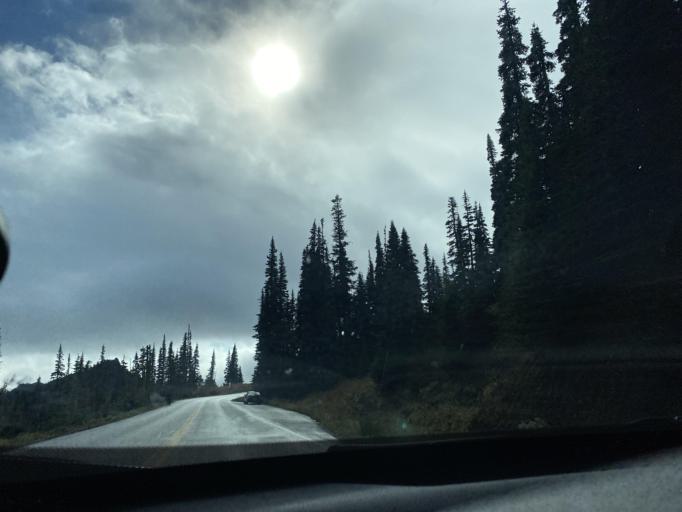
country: US
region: Washington
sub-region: Clallam County
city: Port Angeles
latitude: 47.9756
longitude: -123.4761
